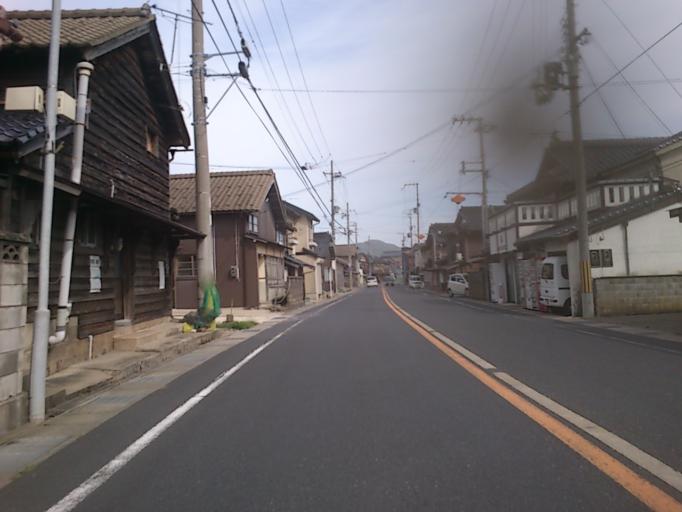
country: JP
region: Kyoto
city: Miyazu
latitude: 35.6882
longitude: 135.0208
